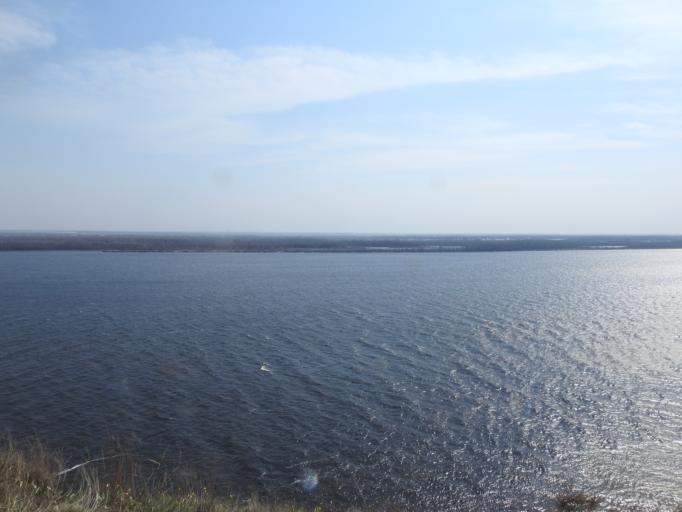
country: RU
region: Saratov
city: Voskresenskoye
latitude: 51.7916
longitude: 46.8537
